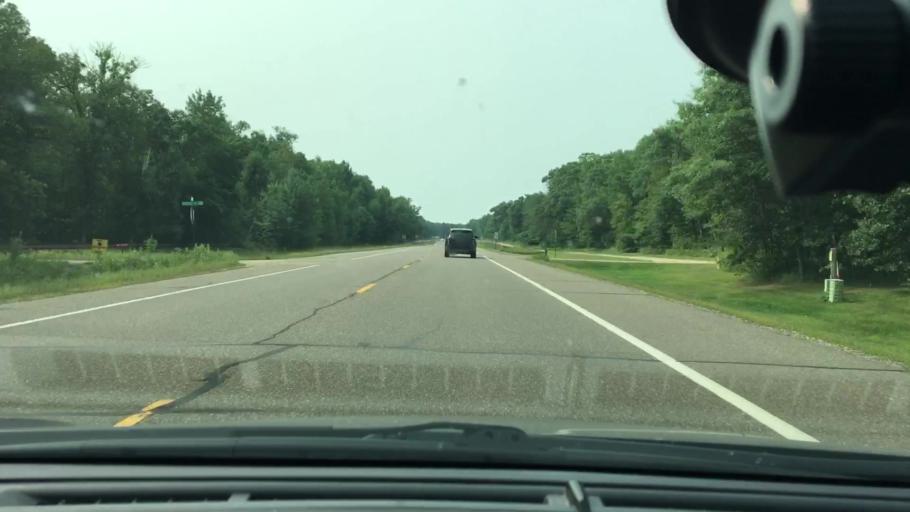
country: US
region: Minnesota
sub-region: Crow Wing County
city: Breezy Point
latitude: 46.5035
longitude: -94.1408
